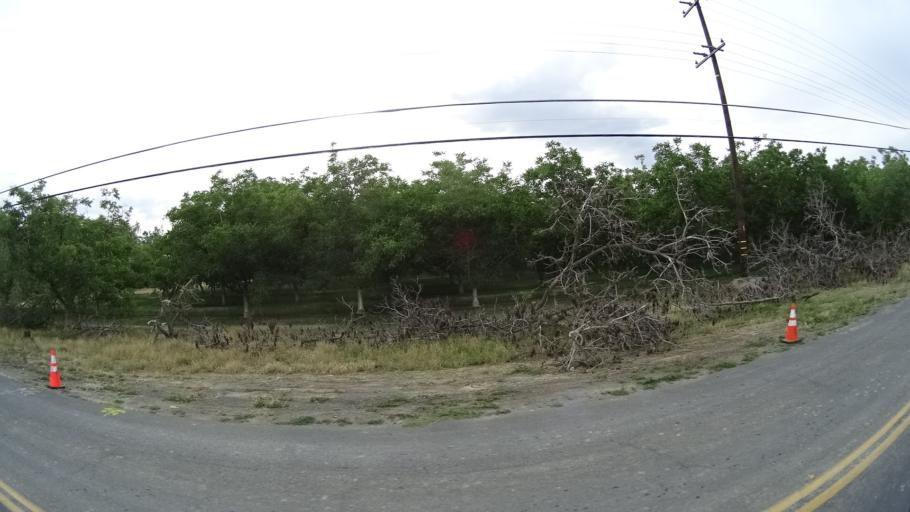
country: US
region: California
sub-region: Kings County
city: Armona
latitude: 36.3419
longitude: -119.6910
